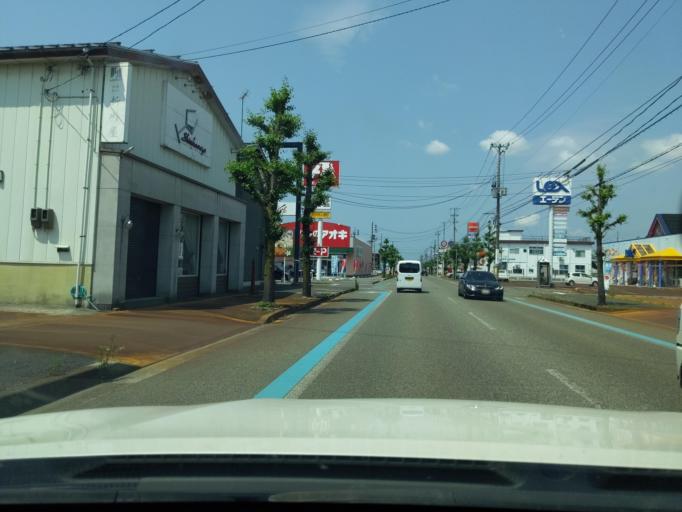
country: JP
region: Niigata
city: Nagaoka
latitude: 37.4271
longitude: 138.8498
